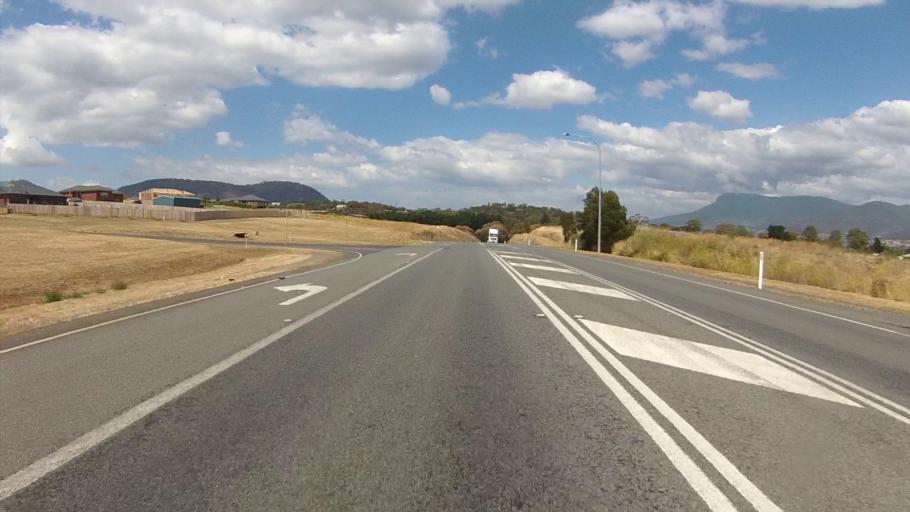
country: AU
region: Tasmania
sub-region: Brighton
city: Old Beach
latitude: -42.7620
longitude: 147.2689
